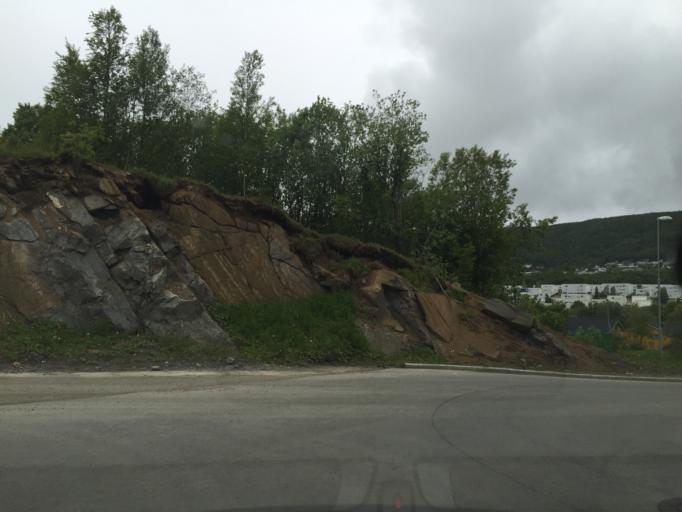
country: NO
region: Nordland
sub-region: Bodo
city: Lopsmarka
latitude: 67.2797
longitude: 14.5449
